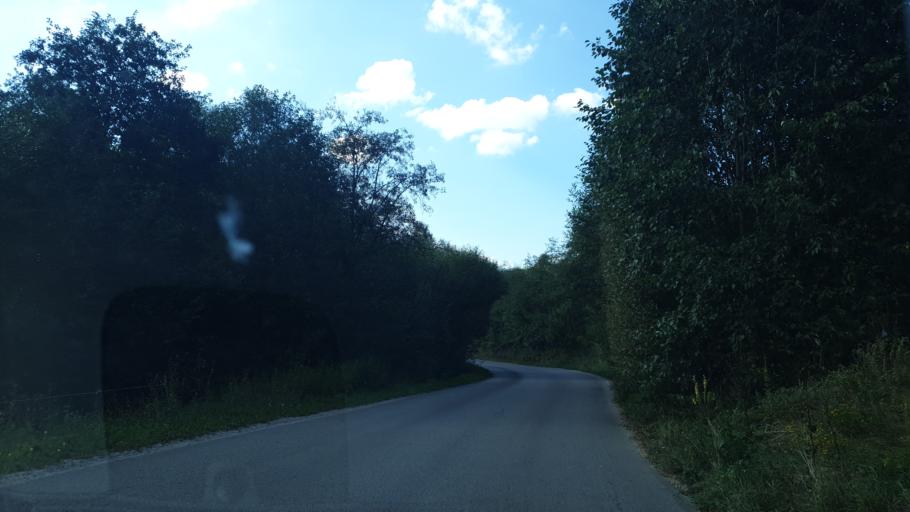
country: RS
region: Central Serbia
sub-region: Zlatiborski Okrug
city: Nova Varos
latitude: 43.4378
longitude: 19.8648
